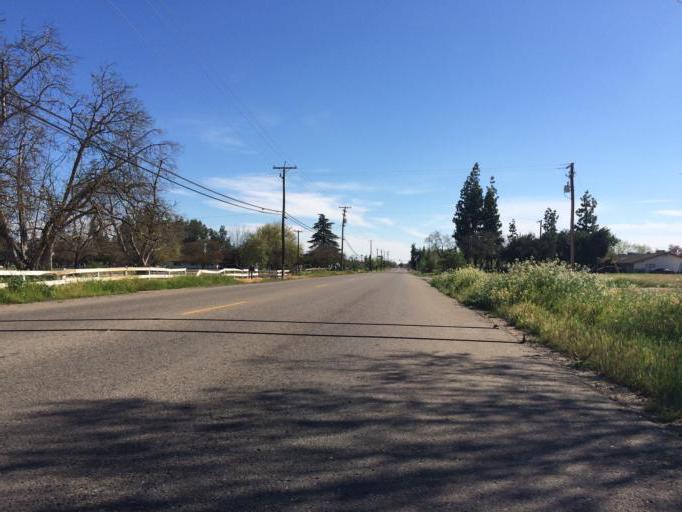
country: US
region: California
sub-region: Fresno County
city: Clovis
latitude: 36.8566
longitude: -119.6841
